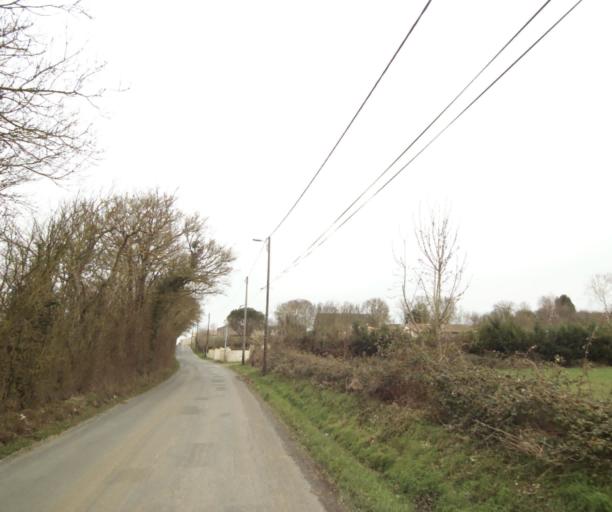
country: FR
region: Poitou-Charentes
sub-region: Departement des Deux-Sevres
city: Magne
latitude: 46.3301
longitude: -0.5238
